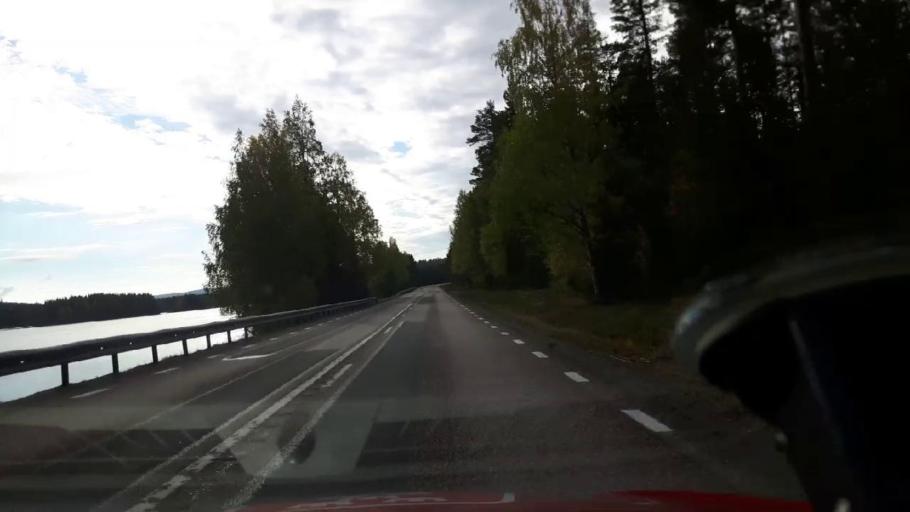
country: SE
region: Gaevleborg
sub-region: Ljusdals Kommun
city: Farila
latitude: 61.9657
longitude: 15.3544
